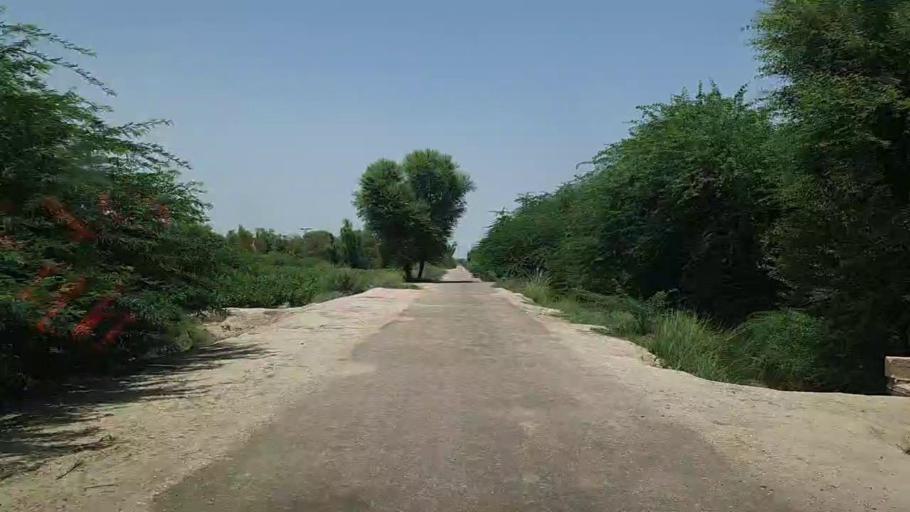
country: PK
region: Sindh
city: Pad Idan
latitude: 26.7418
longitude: 68.3134
